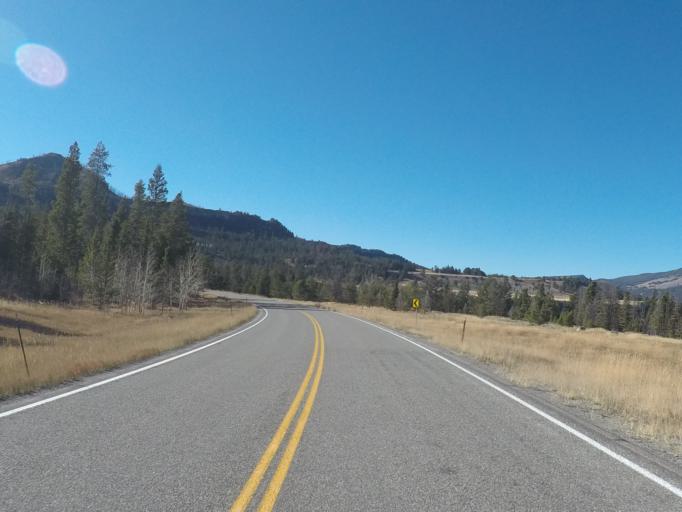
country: US
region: Montana
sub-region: Carbon County
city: Red Lodge
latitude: 44.8355
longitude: -109.4856
